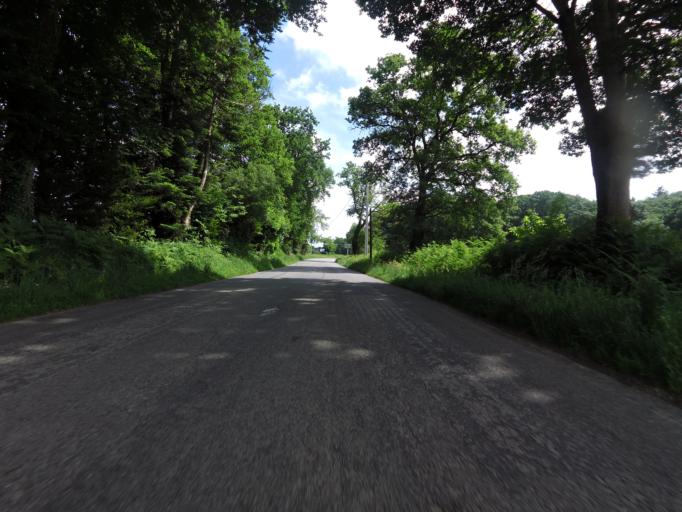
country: FR
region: Brittany
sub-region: Departement du Morbihan
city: Malansac
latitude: 47.6899
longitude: -2.3048
